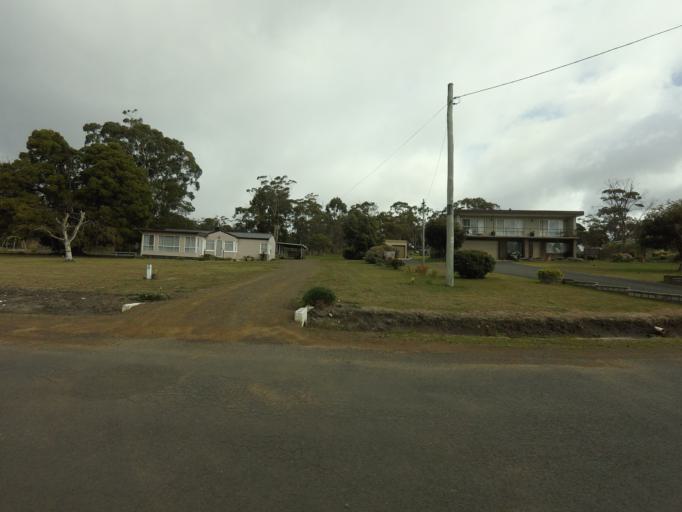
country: AU
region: Tasmania
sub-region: Sorell
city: Sorell
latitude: -42.5269
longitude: 147.9014
